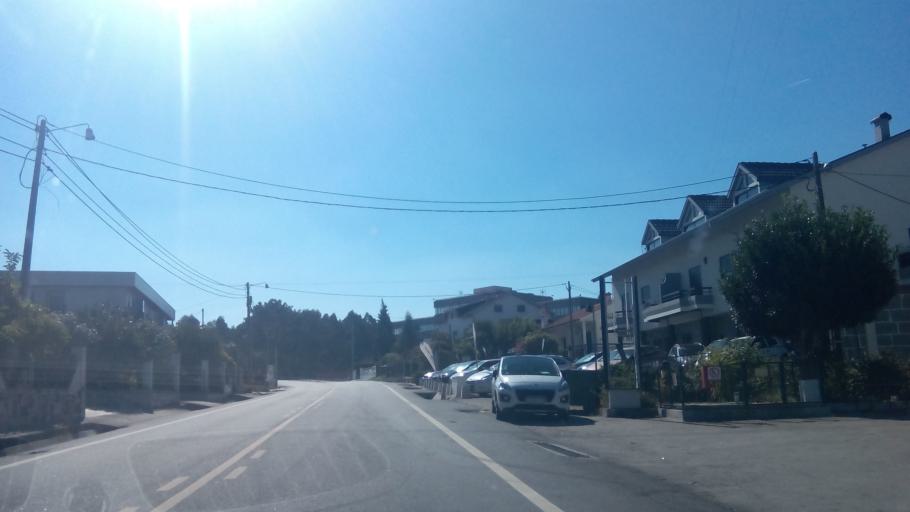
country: PT
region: Porto
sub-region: Lousada
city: Meinedo
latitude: 41.2553
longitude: -8.2133
